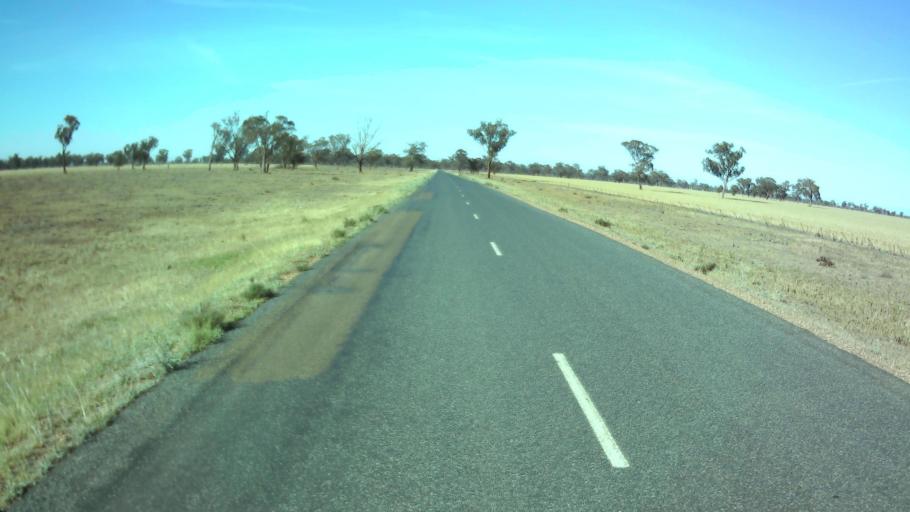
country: AU
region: New South Wales
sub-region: Weddin
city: Grenfell
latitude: -34.0512
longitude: 147.9189
